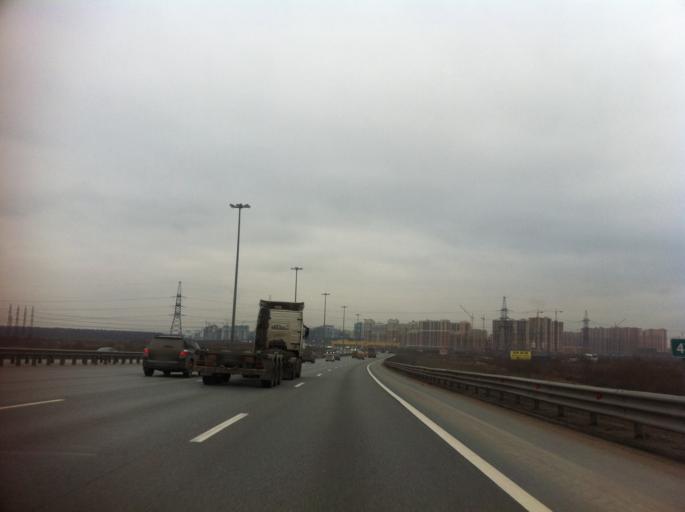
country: RU
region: St.-Petersburg
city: Krasnogvargeisky
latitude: 59.9286
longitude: 30.5341
